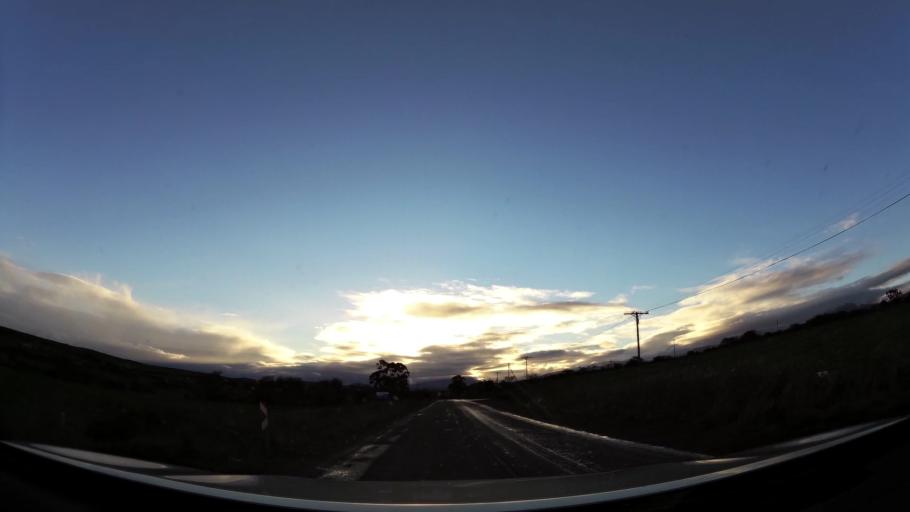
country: ZA
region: Western Cape
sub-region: Eden District Municipality
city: Riversdale
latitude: -34.0812
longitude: 20.9331
